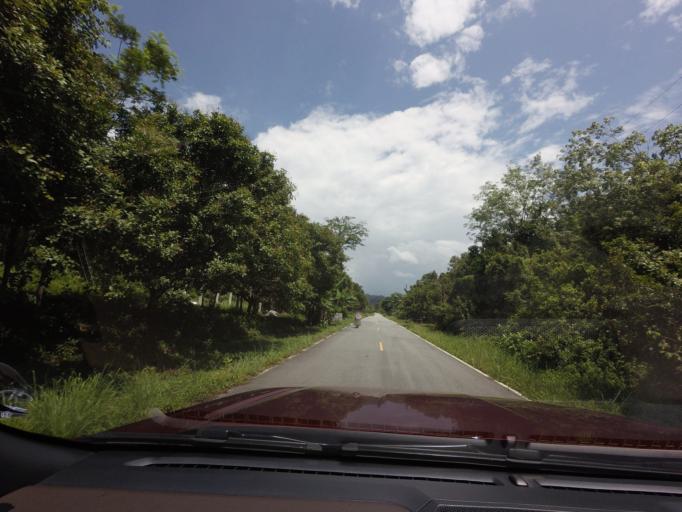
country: TH
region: Narathiwat
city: Chanae
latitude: 6.0838
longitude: 101.6902
